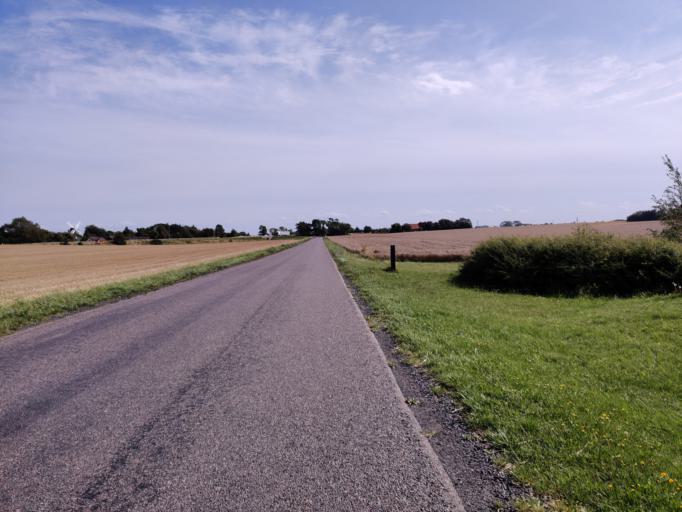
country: DK
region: Zealand
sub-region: Guldborgsund Kommune
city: Nykobing Falster
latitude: 54.6038
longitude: 11.9309
